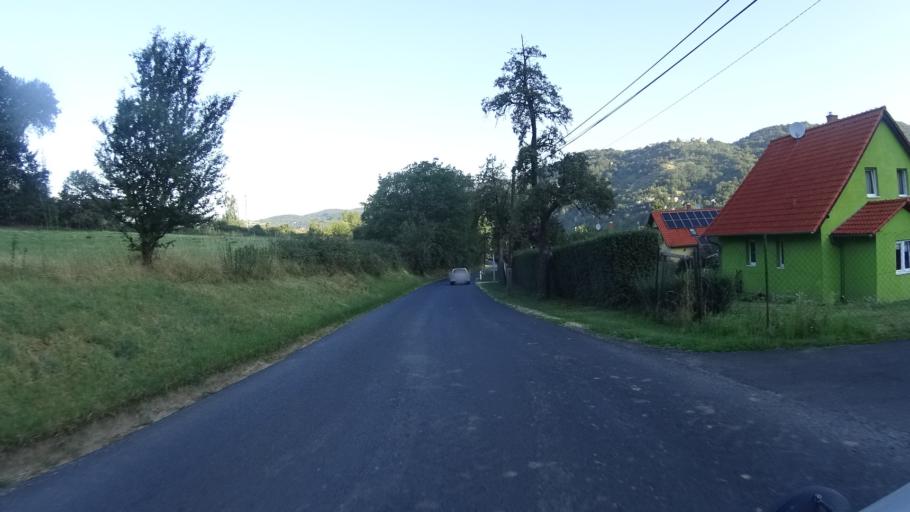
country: CZ
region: Ustecky
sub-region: Okres Usti nad Labem
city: Usti nad Labem
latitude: 50.5918
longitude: 14.0685
